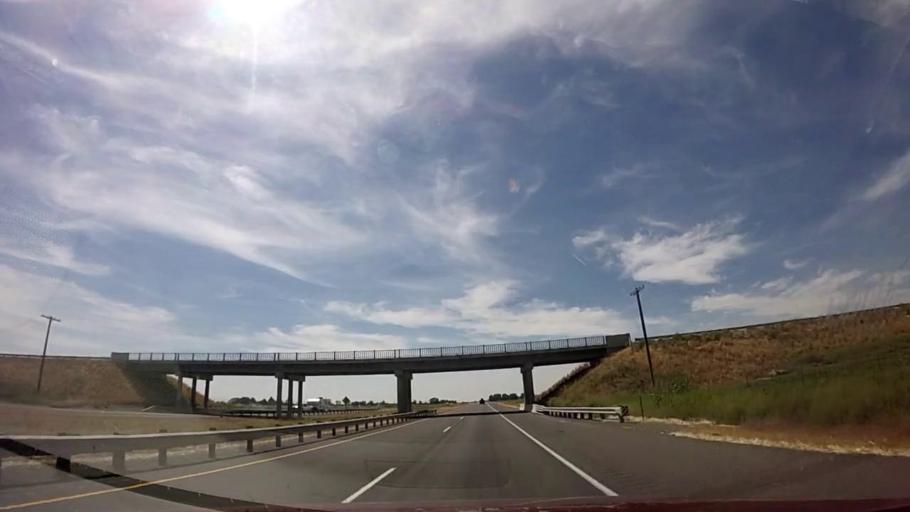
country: US
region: Idaho
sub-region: Minidoka County
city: Rupert
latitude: 42.5689
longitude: -113.6688
